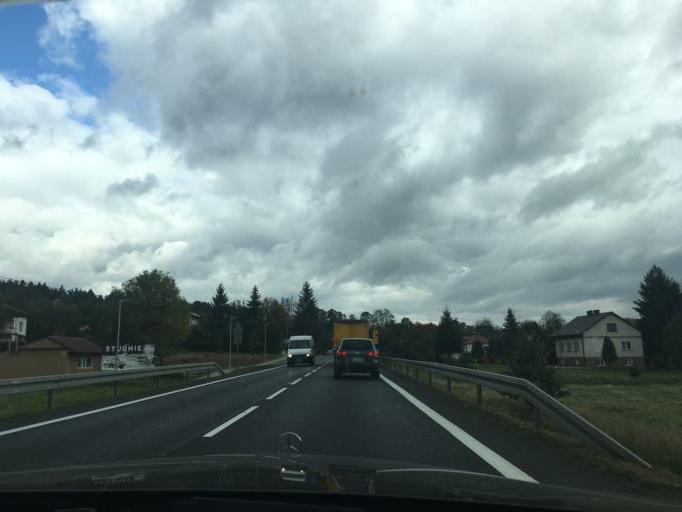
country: PL
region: Subcarpathian Voivodeship
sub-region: Powiat strzyzowski
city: Babica
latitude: 49.9134
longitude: 21.8681
